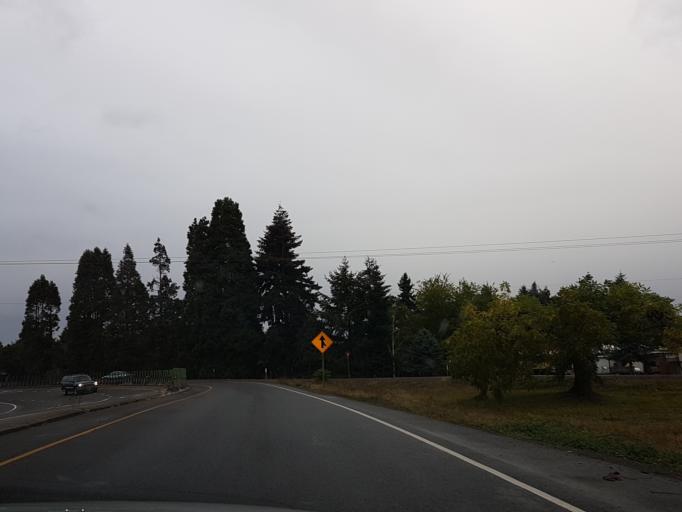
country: US
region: Oregon
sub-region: Linn County
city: Albany
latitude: 44.6301
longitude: -123.0640
